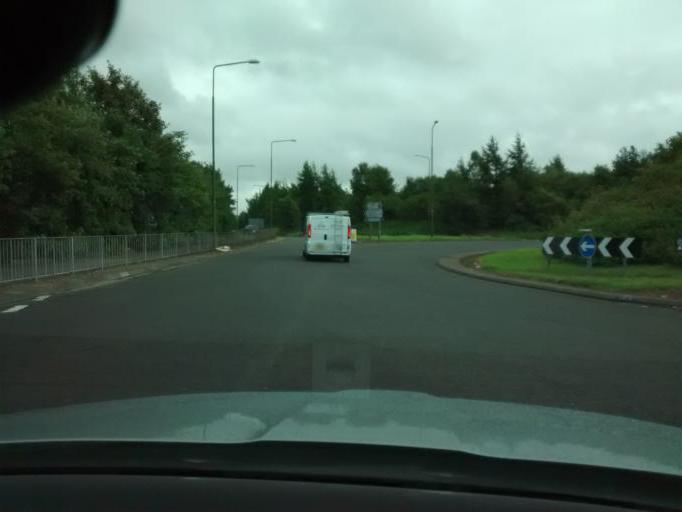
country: GB
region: Scotland
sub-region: West Lothian
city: West Calder
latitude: 55.8905
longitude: -3.5702
